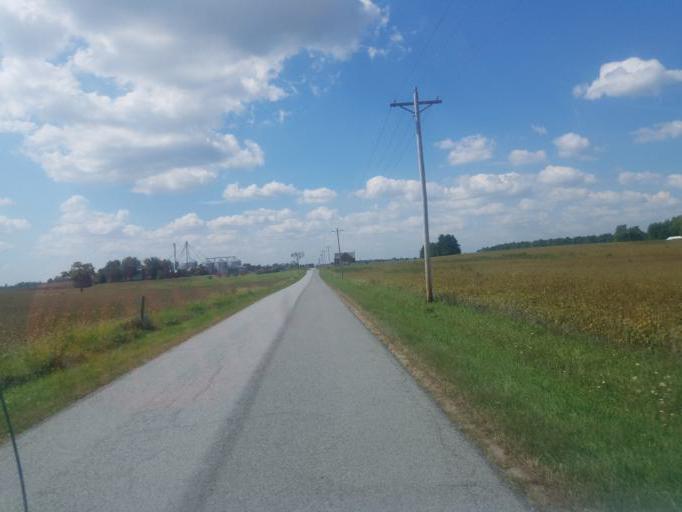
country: US
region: Ohio
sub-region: Hardin County
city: Ada
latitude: 40.6520
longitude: -83.9143
